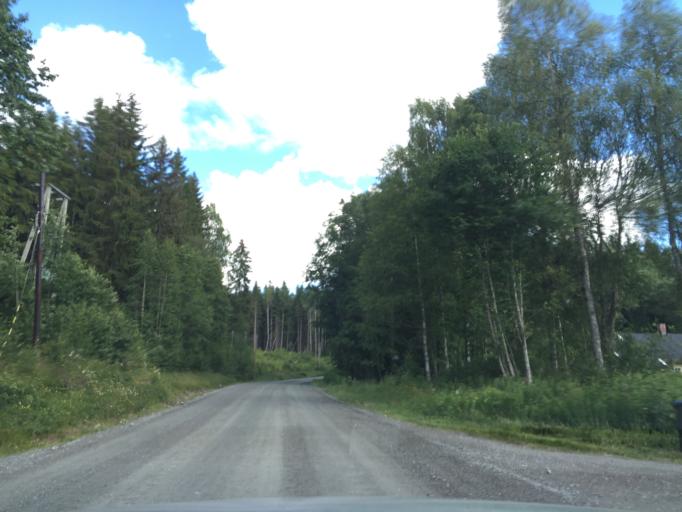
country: NO
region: Hedmark
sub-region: Kongsvinger
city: Spetalen
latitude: 60.2424
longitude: 11.8781
